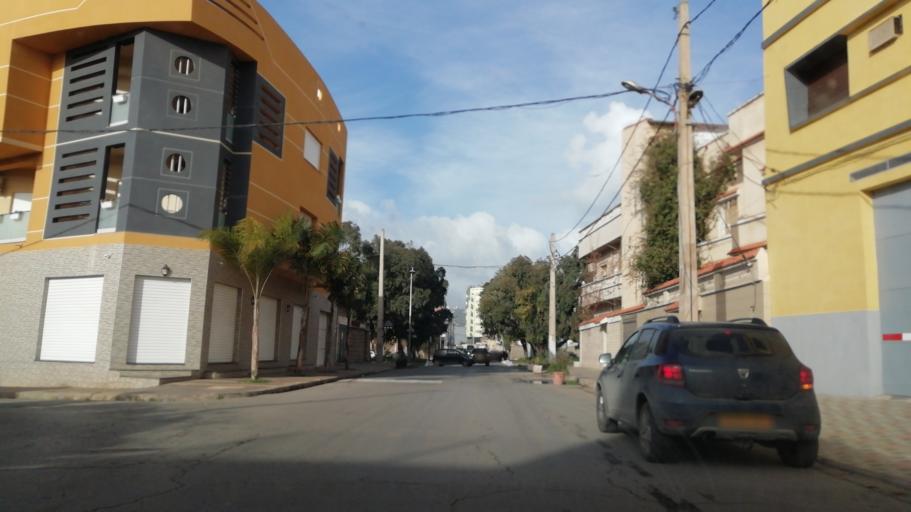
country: DZ
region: Oran
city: Oran
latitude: 35.6959
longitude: -0.6184
